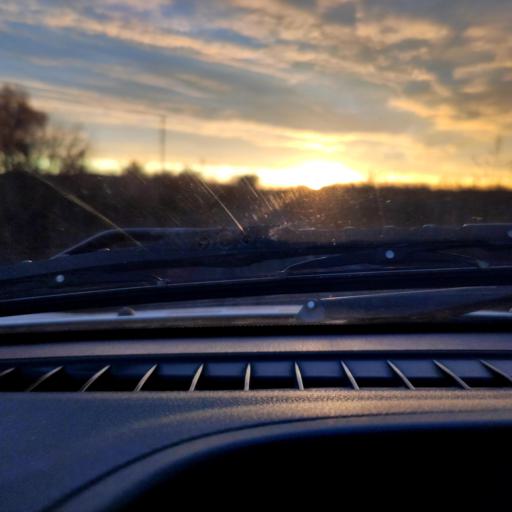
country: RU
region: Samara
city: Tol'yatti
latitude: 53.5960
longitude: 49.4786
